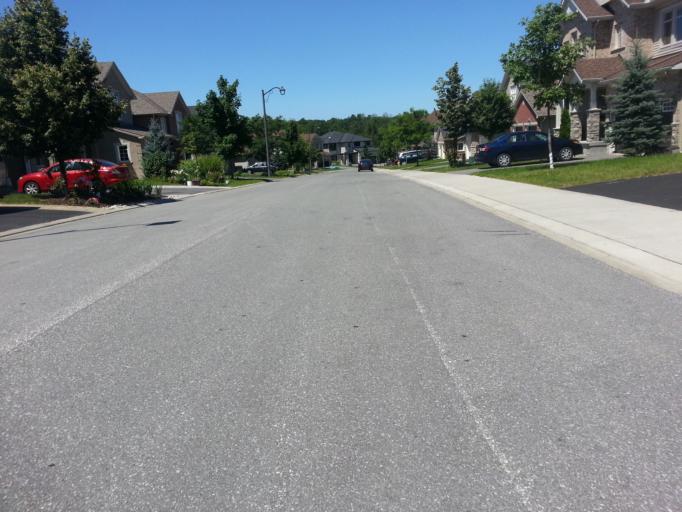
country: CA
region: Ontario
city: Bells Corners
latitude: 45.3225
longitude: -75.9341
